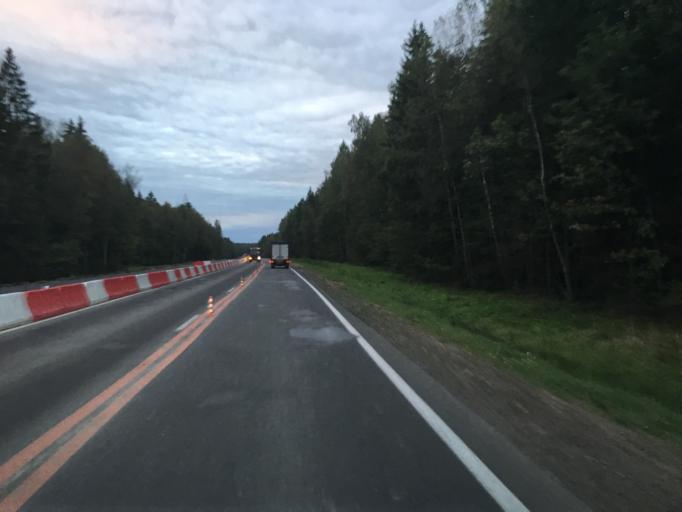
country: RU
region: Kaluga
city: Detchino
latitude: 54.6957
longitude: 36.2948
